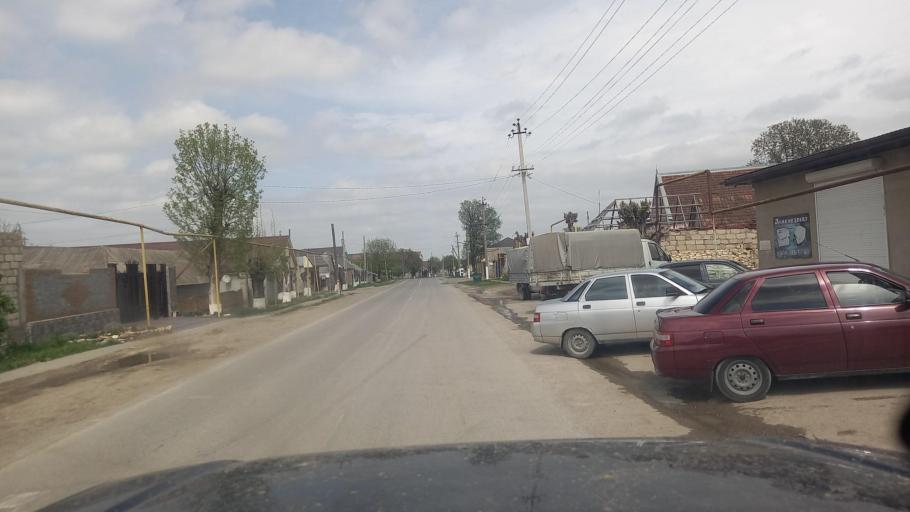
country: RU
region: Kabardino-Balkariya
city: Sarmakovo
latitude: 43.7373
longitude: 43.1813
